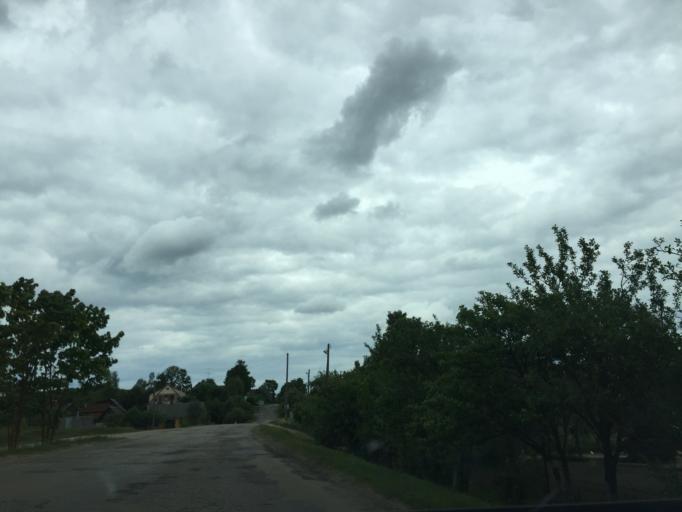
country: LV
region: Dagda
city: Dagda
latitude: 56.0853
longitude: 27.5315
